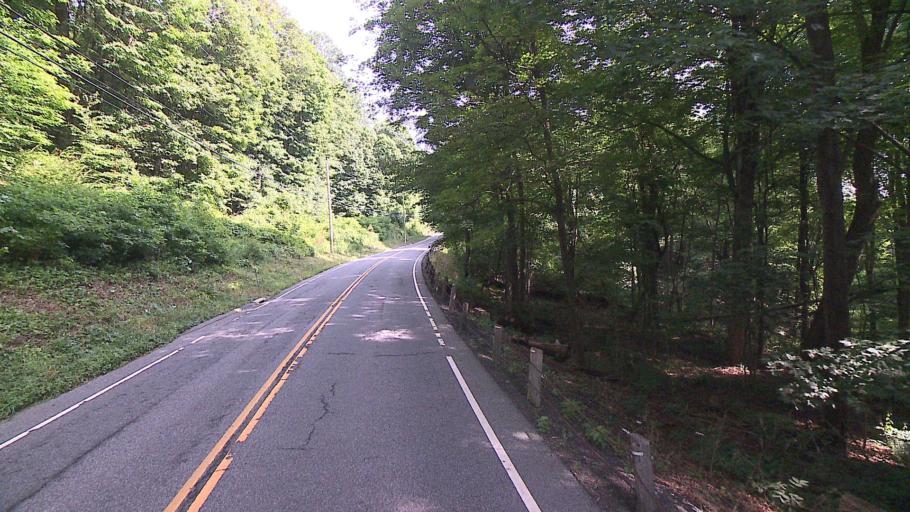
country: US
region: Connecticut
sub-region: Fairfield County
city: Sherman
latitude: 41.5449
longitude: -73.4996
